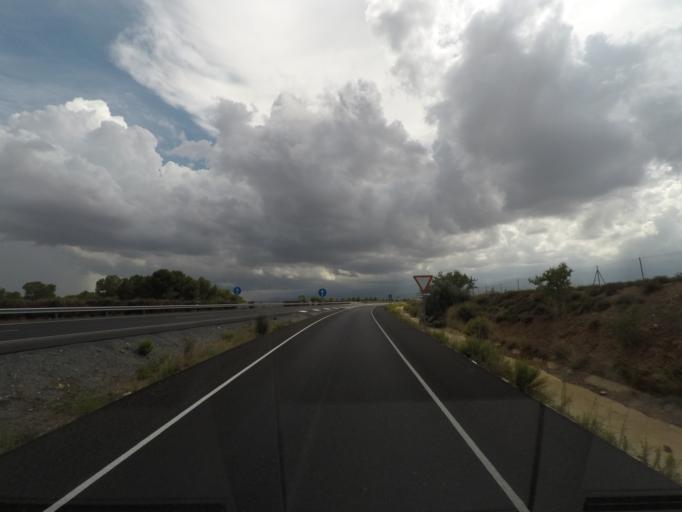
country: ES
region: Andalusia
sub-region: Provincia de Granada
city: Albunan
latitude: 37.2606
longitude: -3.0837
